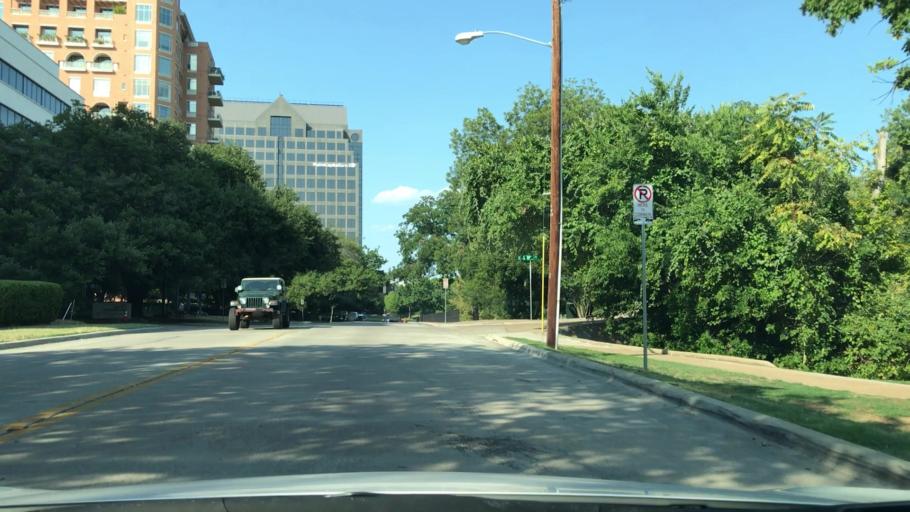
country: US
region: Texas
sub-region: Dallas County
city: Dallas
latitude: 32.8023
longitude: -96.8082
